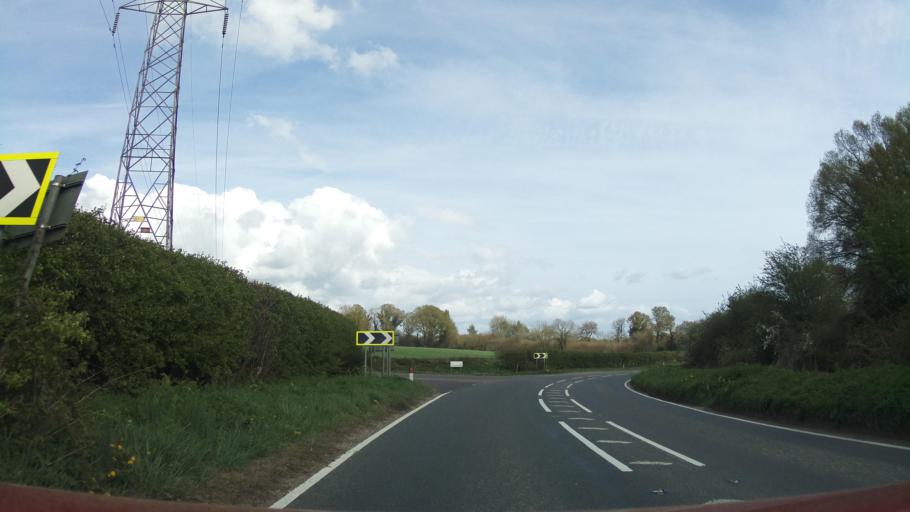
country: GB
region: England
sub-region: Hampshire
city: Compton
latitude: 51.0155
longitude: -1.3577
